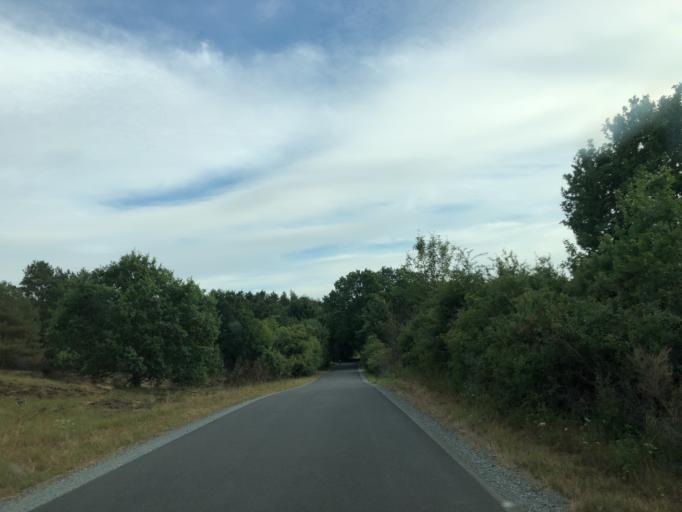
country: DK
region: South Denmark
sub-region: Vejle Kommune
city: Egtved
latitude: 55.6658
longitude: 9.2597
